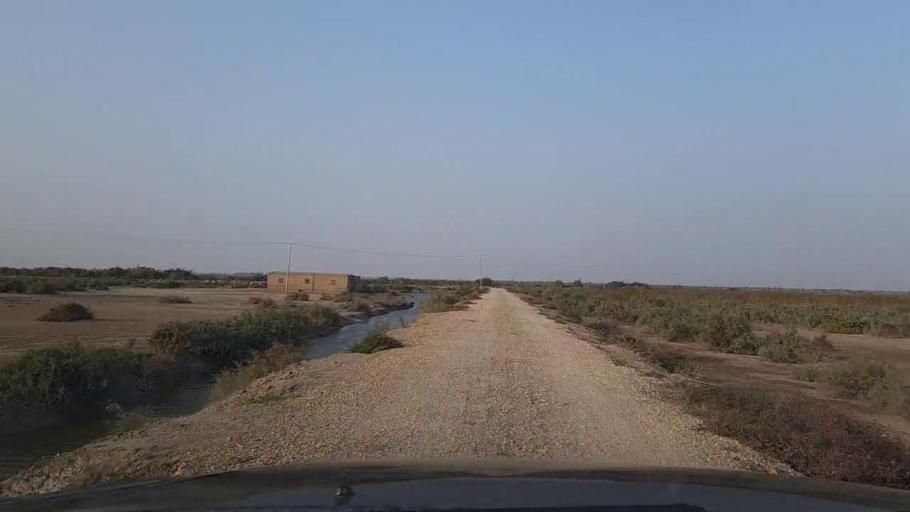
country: PK
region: Sindh
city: Mirpur Sakro
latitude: 24.4134
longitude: 67.7322
